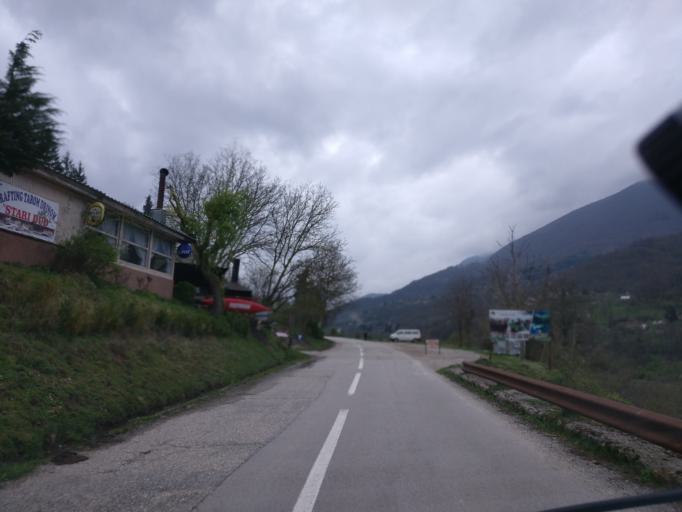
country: BA
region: Republika Srpska
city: Foca
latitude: 43.4476
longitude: 18.7557
